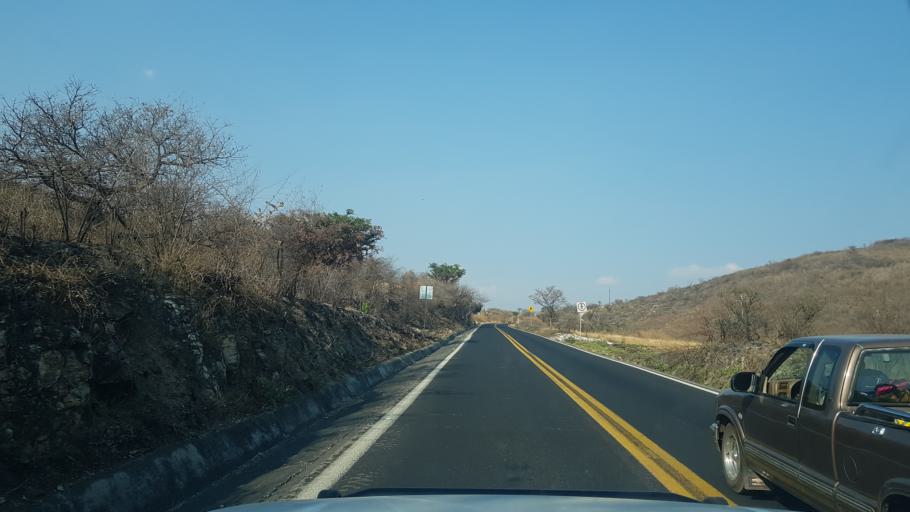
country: MX
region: Puebla
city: Calmeca
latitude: 18.6423
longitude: -98.6077
